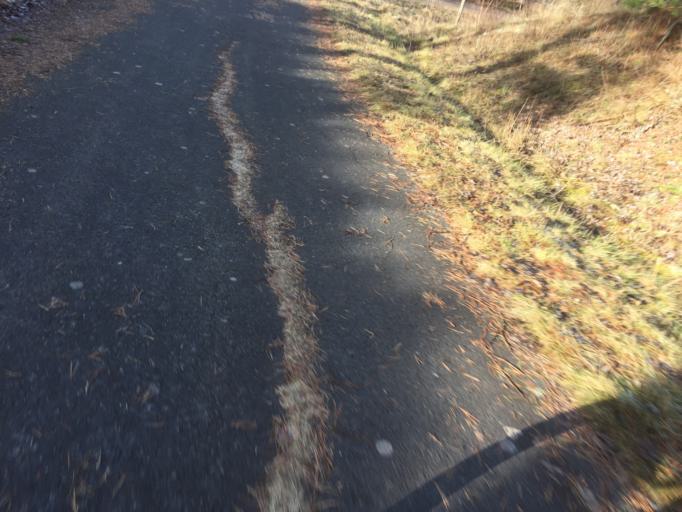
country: SE
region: Joenkoeping
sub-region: Aneby Kommun
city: Aneby
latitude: 57.8269
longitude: 14.8237
